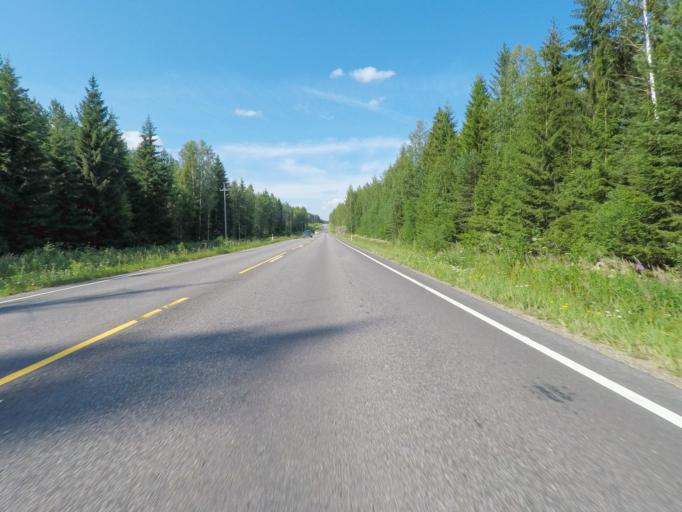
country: FI
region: Southern Savonia
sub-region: Mikkeli
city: Puumala
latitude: 61.5475
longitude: 28.1817
